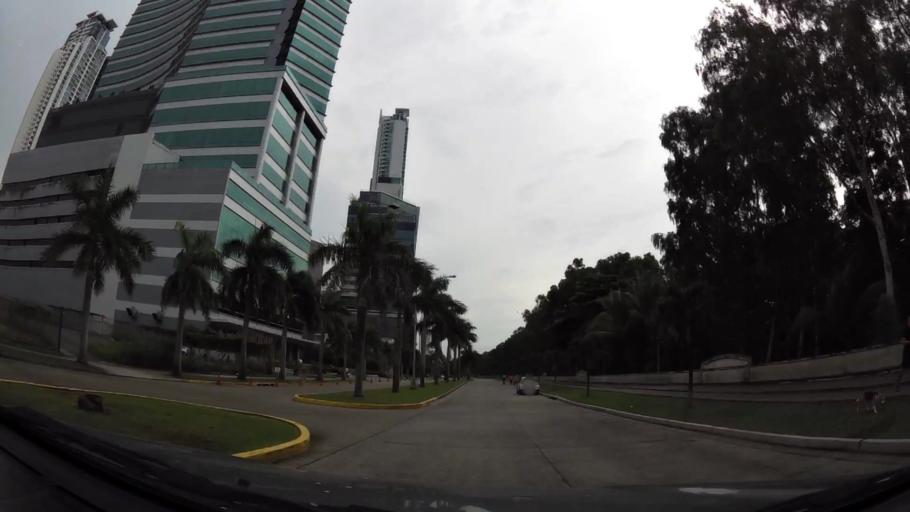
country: PA
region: Panama
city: San Miguelito
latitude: 9.0077
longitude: -79.4779
